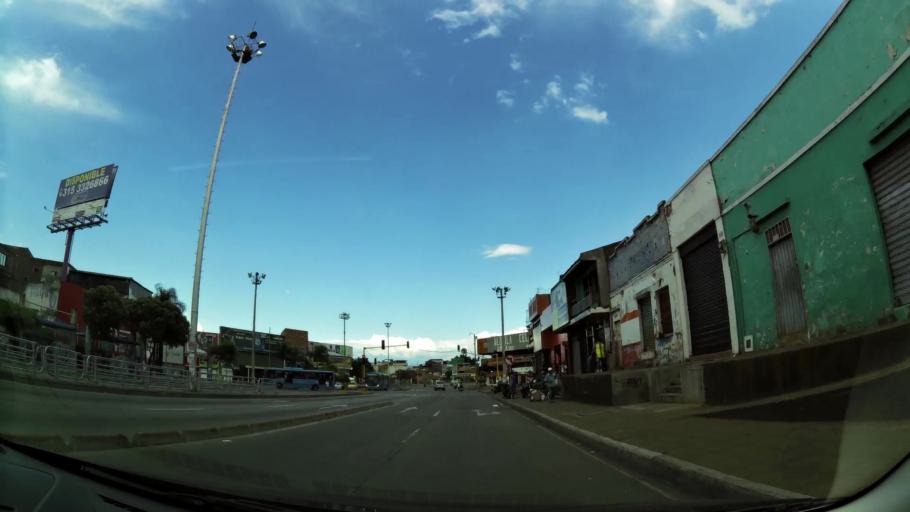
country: CO
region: Valle del Cauca
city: Cali
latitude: 3.4425
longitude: -76.5266
